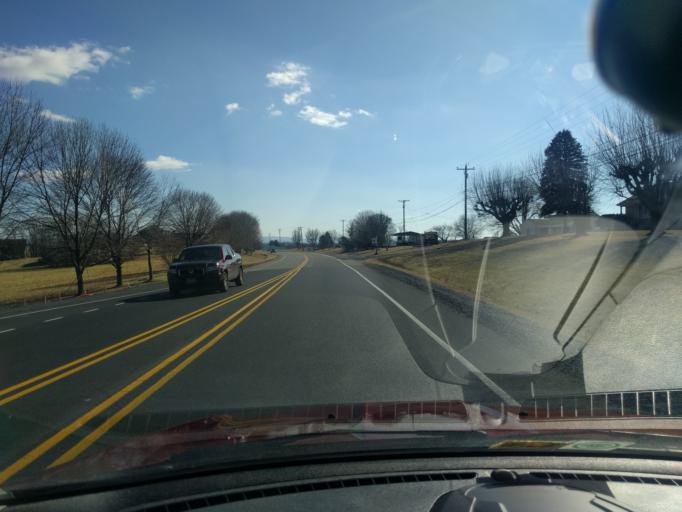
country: US
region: Virginia
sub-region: Rockingham County
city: Bridgewater
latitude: 38.3722
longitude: -78.9516
